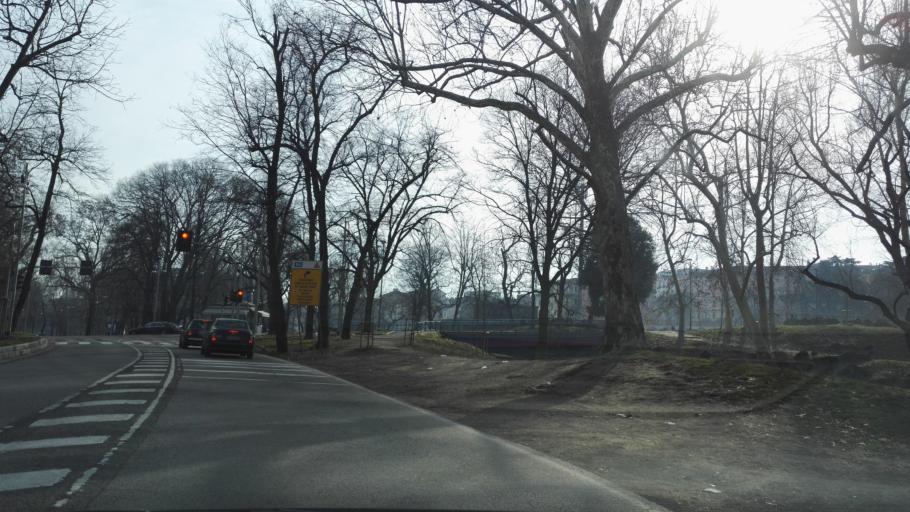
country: IT
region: Lombardy
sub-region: Citta metropolitana di Milano
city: Milano
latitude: 45.4724
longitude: 9.1722
